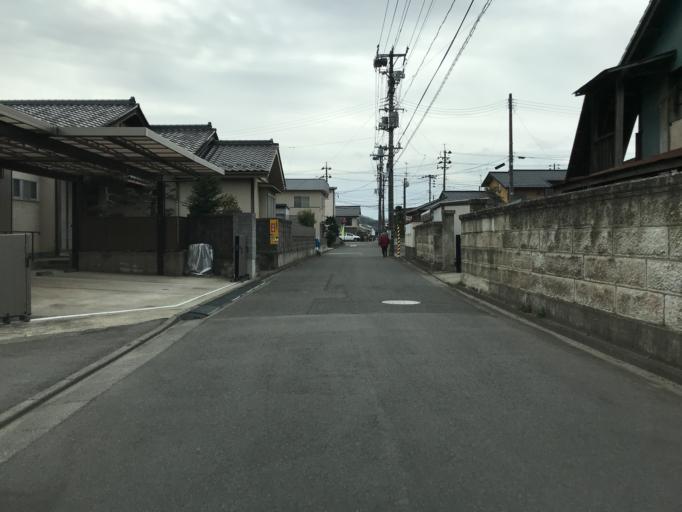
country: JP
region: Fukushima
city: Fukushima-shi
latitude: 37.7572
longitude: 140.4798
